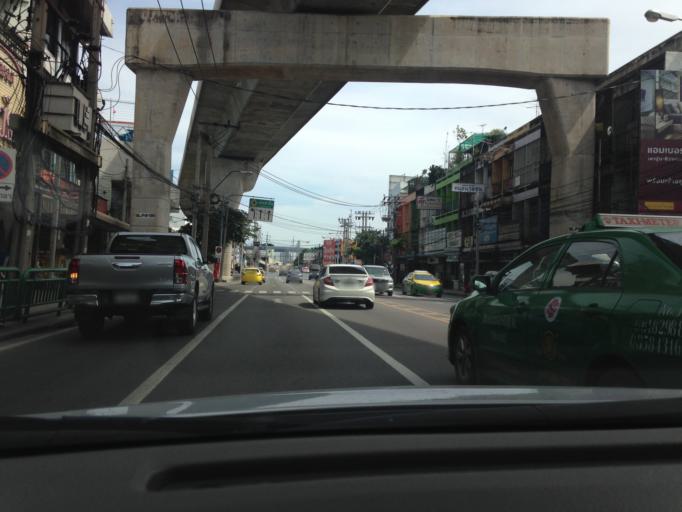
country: TH
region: Bangkok
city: Bang Sue
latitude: 13.8061
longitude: 100.5320
